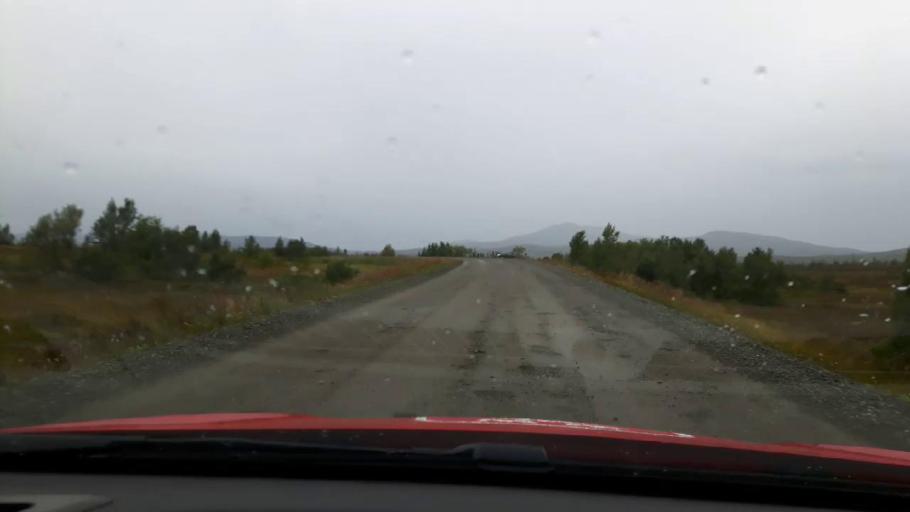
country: NO
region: Nord-Trondelag
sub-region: Meraker
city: Meraker
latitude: 63.6130
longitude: 12.2788
